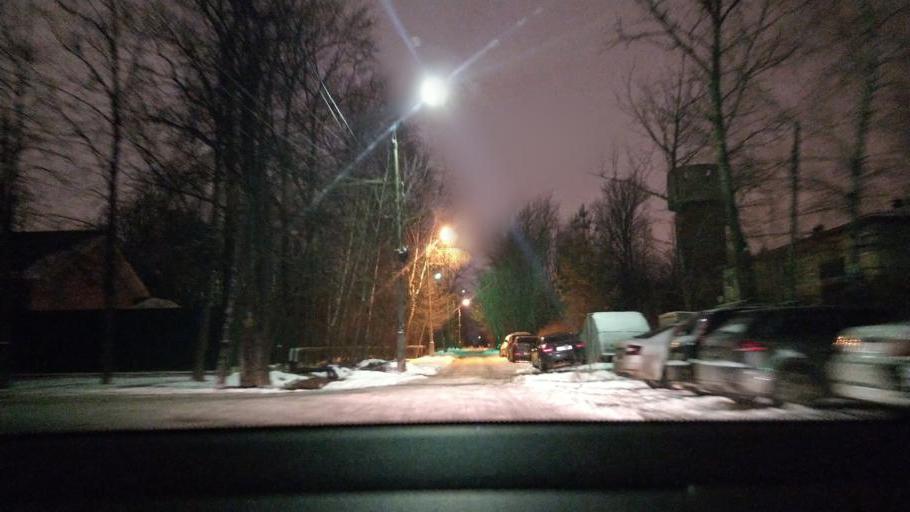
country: RU
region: Moskovskaya
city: Odintsovo
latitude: 55.6584
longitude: 37.2734
